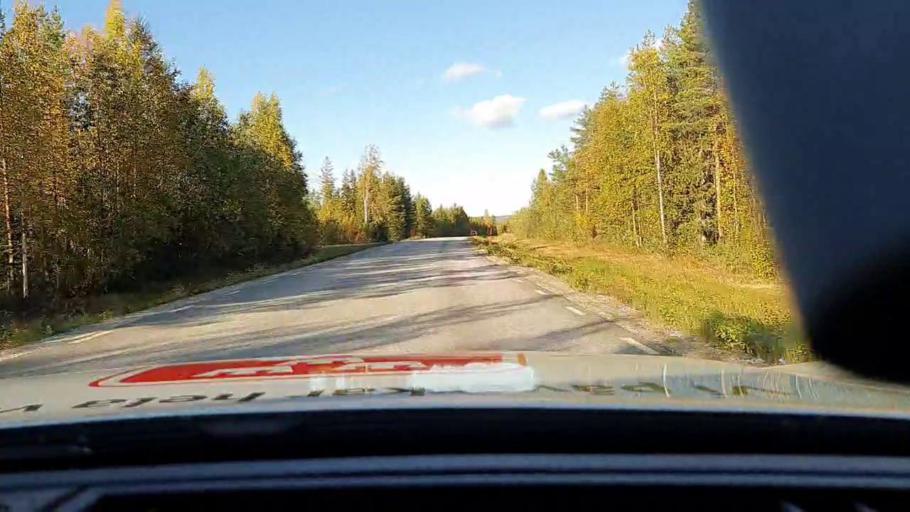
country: SE
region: Norrbotten
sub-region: Pitea Kommun
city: Norrfjarden
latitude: 65.5014
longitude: 21.4764
